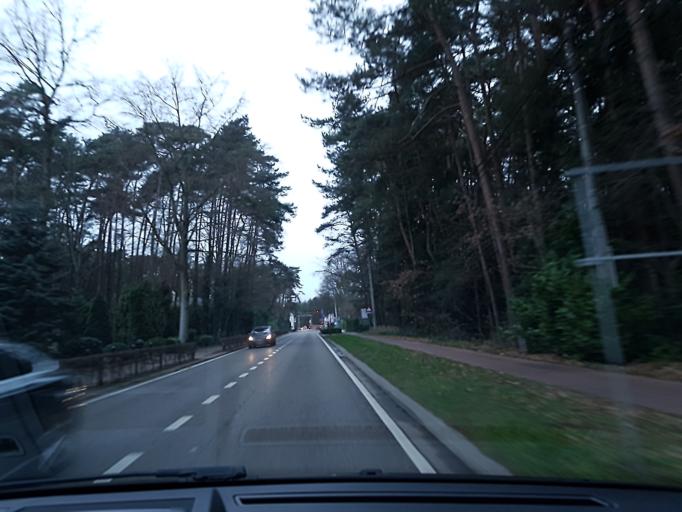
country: BE
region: Flanders
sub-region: Provincie Vlaams-Brabant
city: Keerbergen
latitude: 51.0101
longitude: 4.6011
